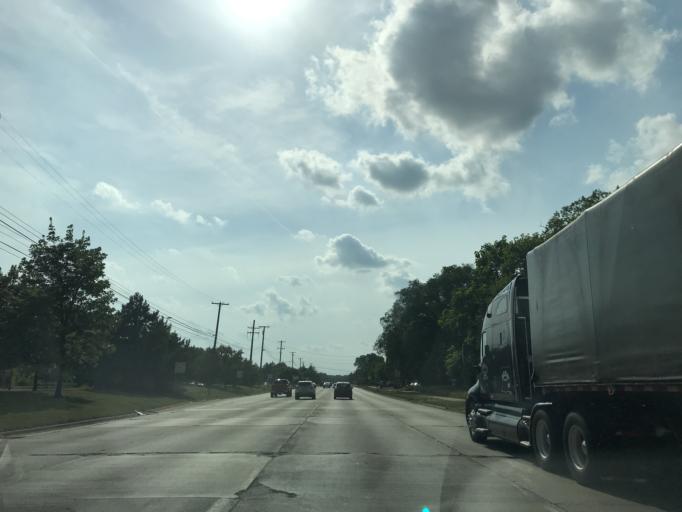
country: US
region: Michigan
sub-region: Wayne County
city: Wayne
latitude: 42.2793
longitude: -83.4276
